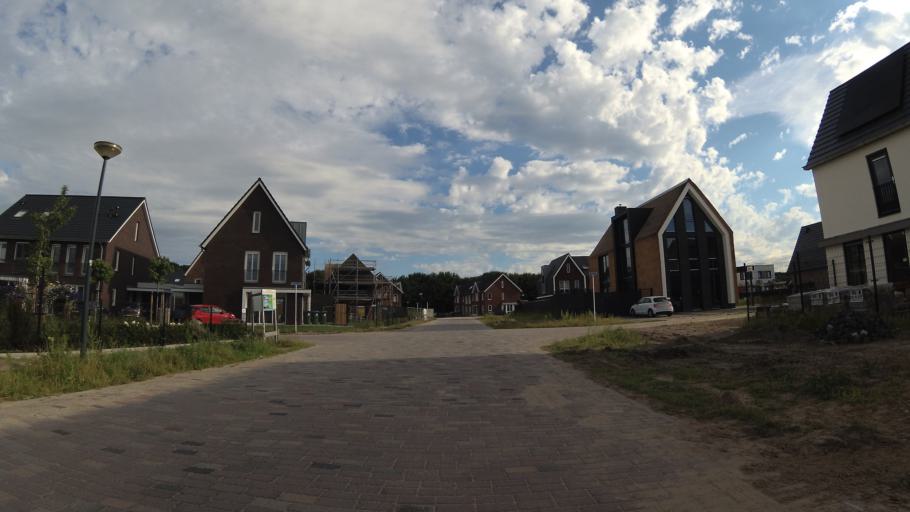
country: NL
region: North Brabant
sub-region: Gemeente Oosterhout
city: Oosterhout
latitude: 51.6488
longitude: 4.8235
